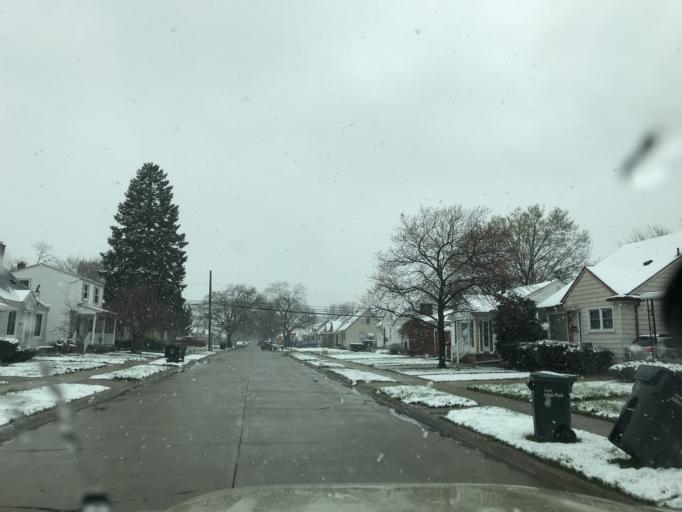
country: US
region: Michigan
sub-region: Wayne County
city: Allen Park
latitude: 42.2630
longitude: -83.1932
